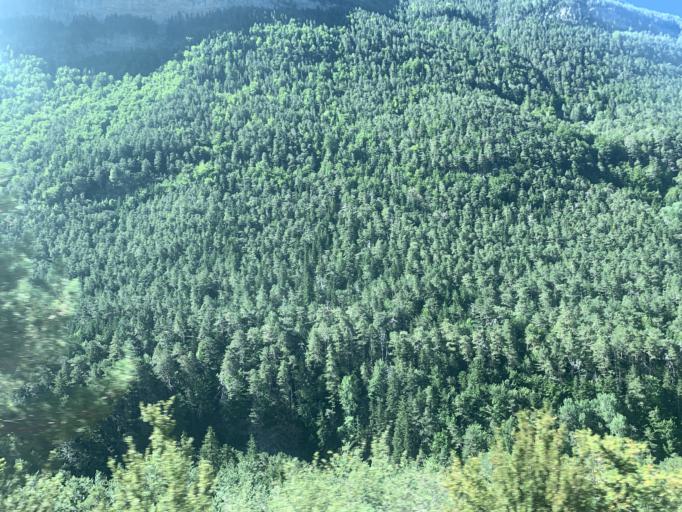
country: ES
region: Aragon
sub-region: Provincia de Huesca
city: Broto
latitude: 42.6544
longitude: -0.0875
